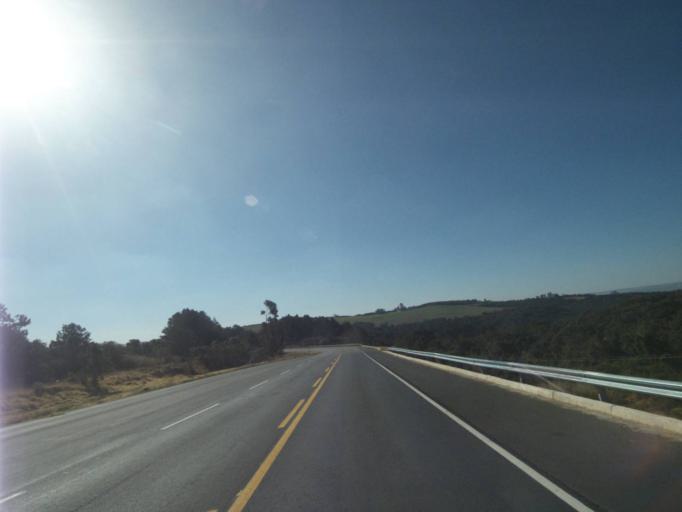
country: BR
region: Parana
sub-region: Tibagi
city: Tibagi
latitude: -24.7935
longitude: -50.4661
